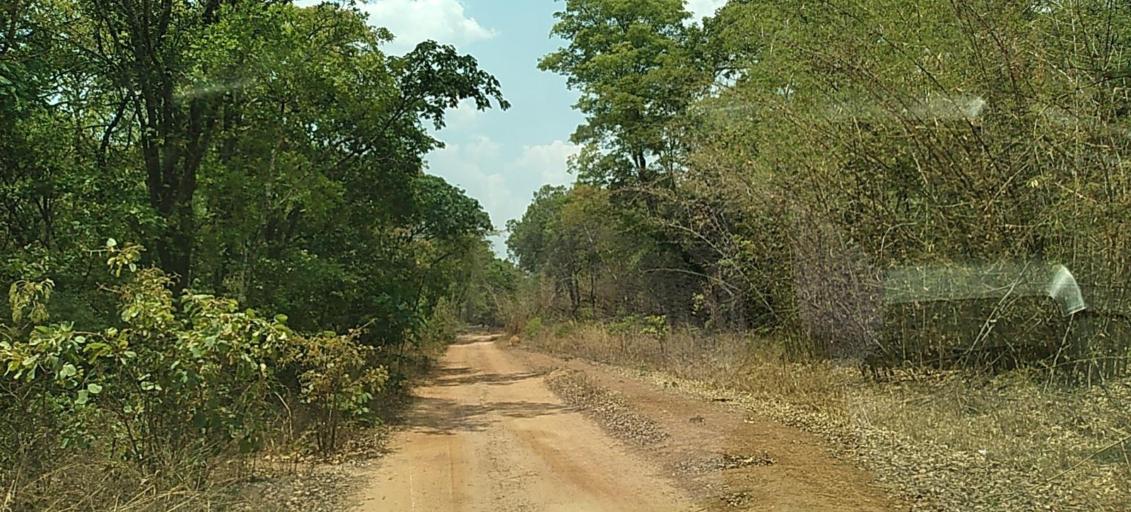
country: ZM
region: Copperbelt
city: Chingola
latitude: -12.8079
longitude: 27.6399
